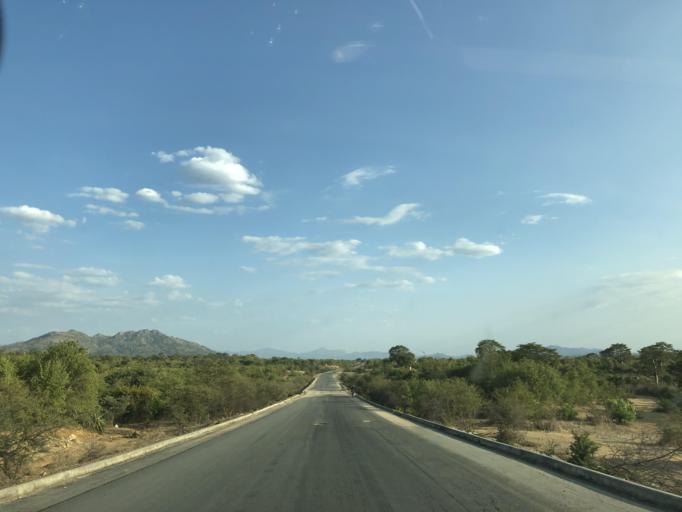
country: AO
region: Huila
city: Caluquembe
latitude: -13.4990
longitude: 13.9142
